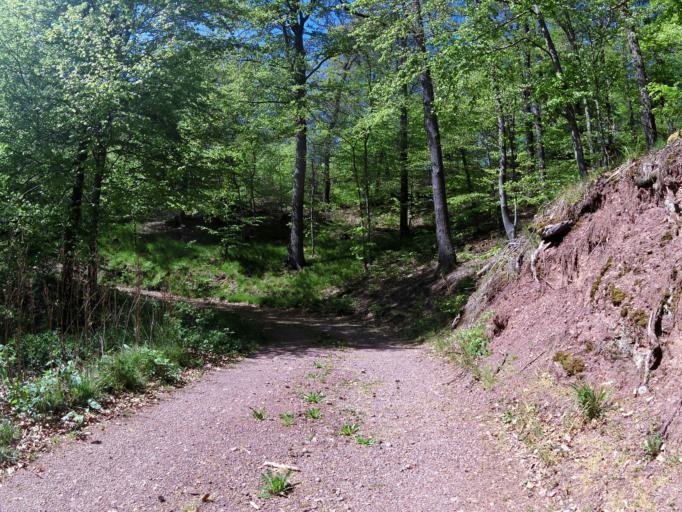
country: DE
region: Thuringia
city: Wolfsburg-Unkeroda
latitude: 50.9634
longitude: 10.2672
